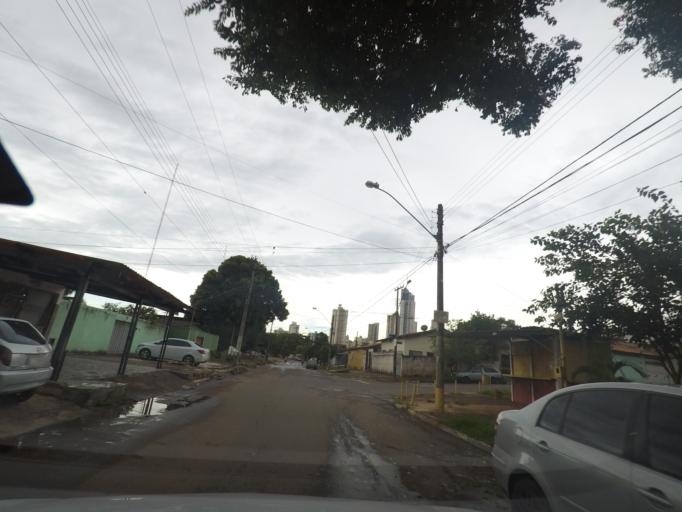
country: BR
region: Goias
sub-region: Goiania
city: Goiania
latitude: -16.7178
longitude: -49.2453
